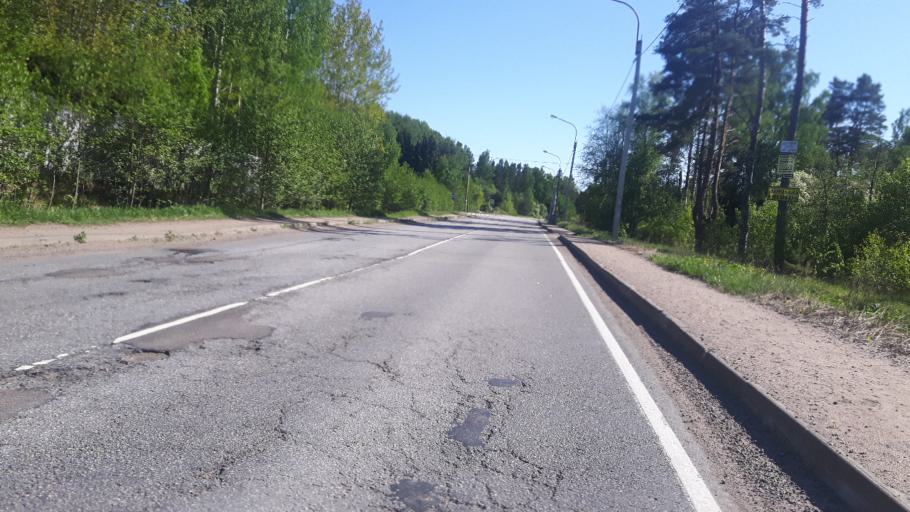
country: RU
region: Leningrad
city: Sosnovyy Bor
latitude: 60.2111
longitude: 29.0062
